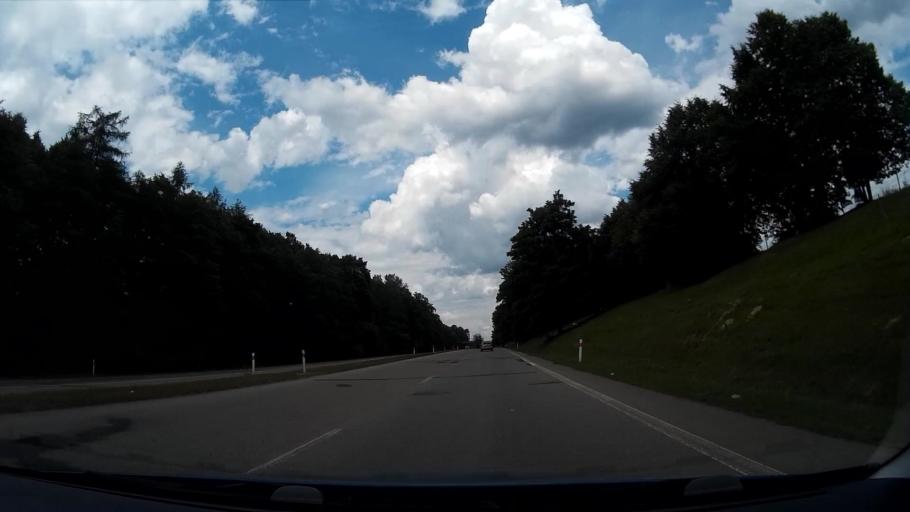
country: CZ
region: South Moravian
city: Troubsko
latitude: 49.2169
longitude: 16.5217
